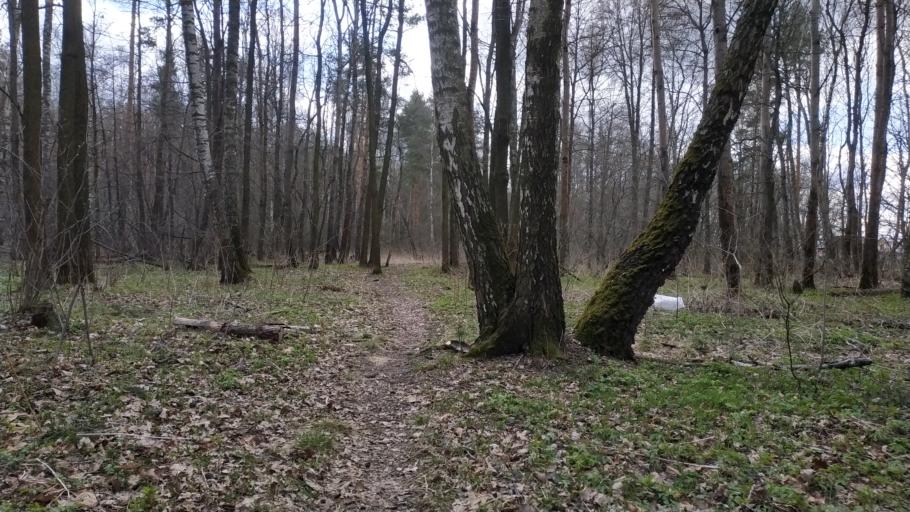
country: RU
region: Moskovskaya
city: Malyshevo
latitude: 55.5495
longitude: 38.3206
